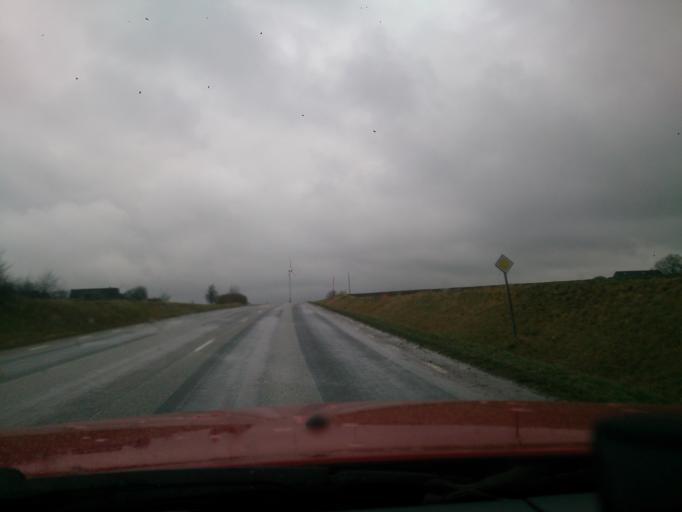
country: SE
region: Skane
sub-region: Ystads Kommun
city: Ystad
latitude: 55.4316
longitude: 13.7188
